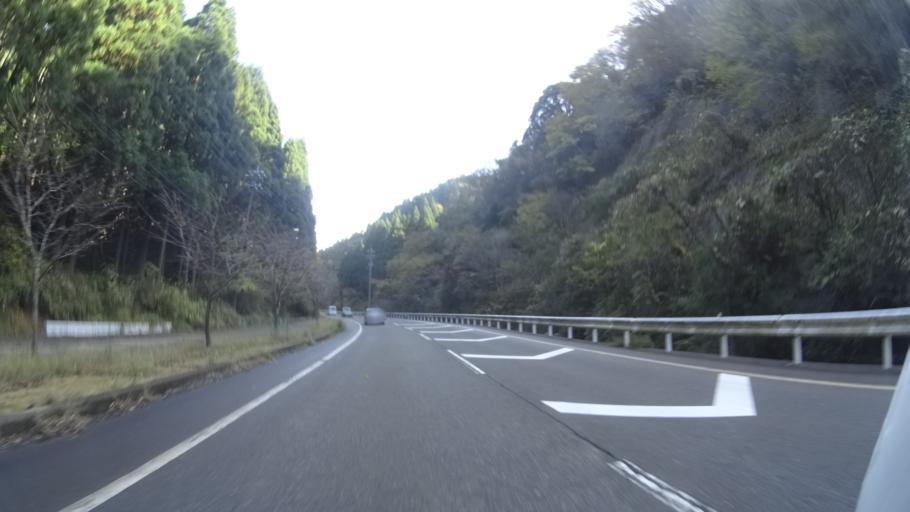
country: JP
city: Asahi
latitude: 35.9575
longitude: 136.0033
